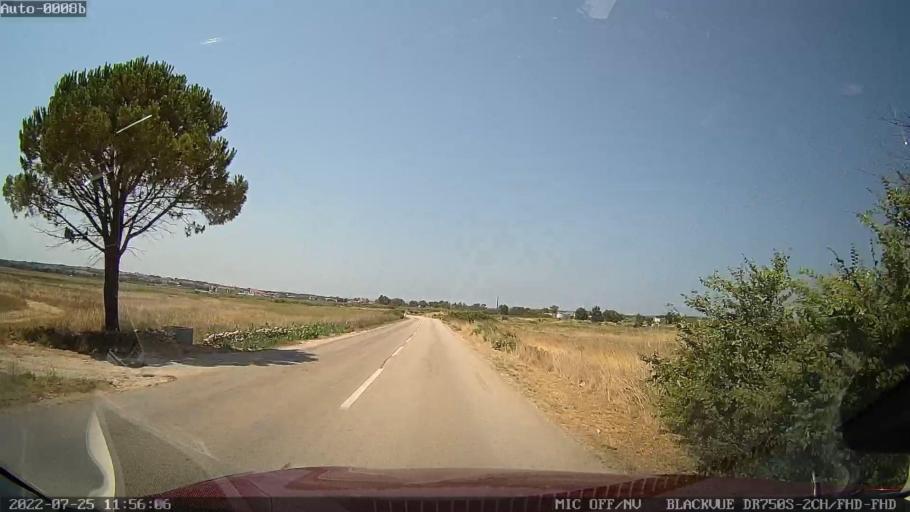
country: HR
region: Zadarska
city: Vrsi
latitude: 44.2523
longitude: 15.2204
